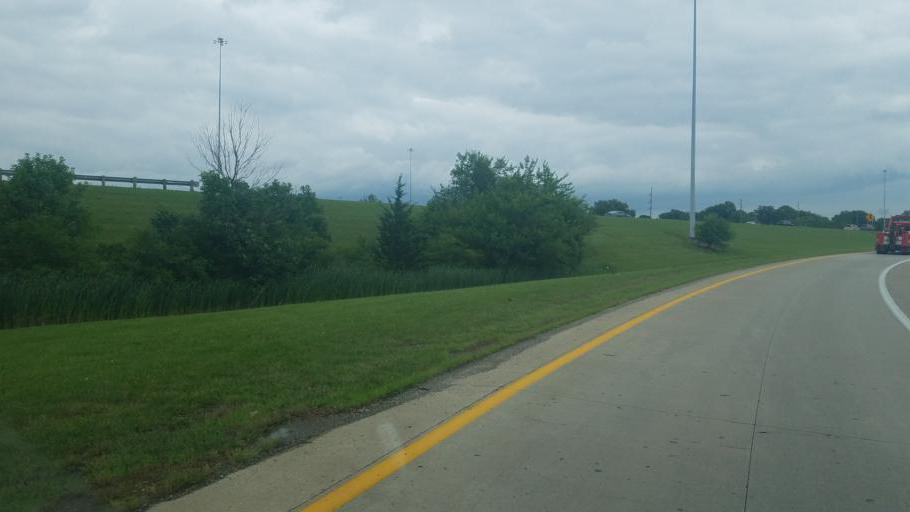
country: US
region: Ohio
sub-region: Franklin County
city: Grove City
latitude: 39.9025
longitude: -83.0761
